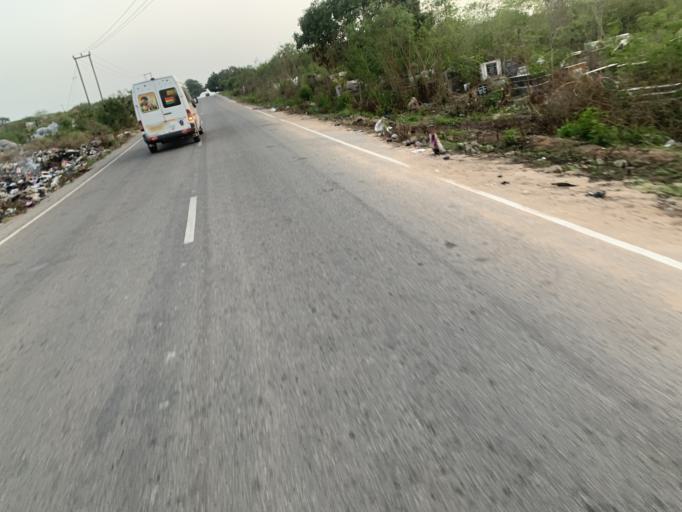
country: GH
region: Central
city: Winneba
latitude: 5.3619
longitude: -0.6092
